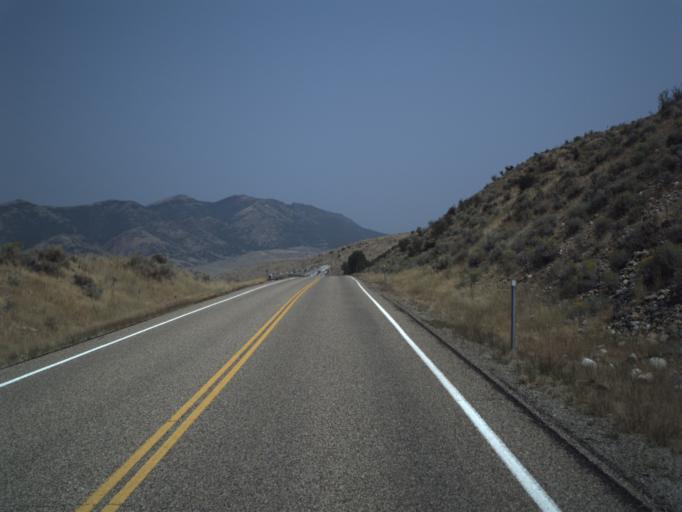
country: US
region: Utah
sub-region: Summit County
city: Summit Park
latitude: 40.9009
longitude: -111.5883
